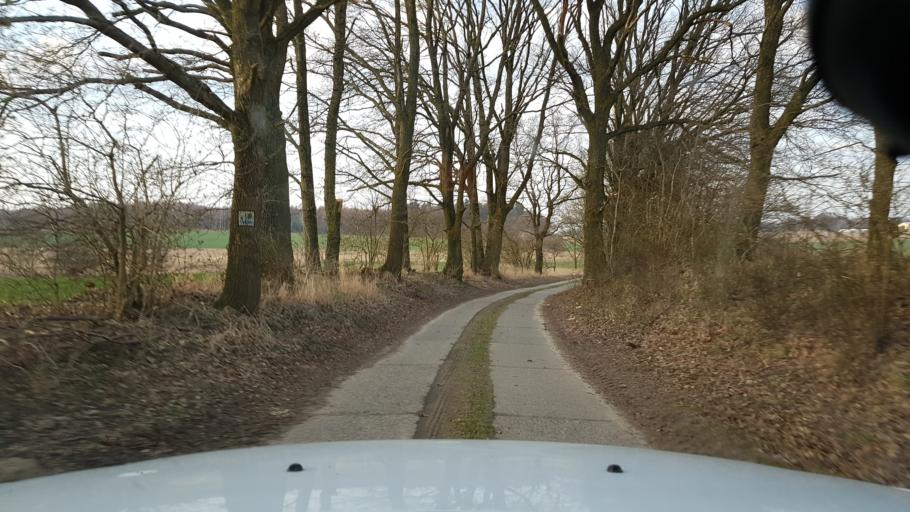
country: PL
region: West Pomeranian Voivodeship
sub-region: Koszalin
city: Koszalin
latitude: 54.0967
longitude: 16.1403
